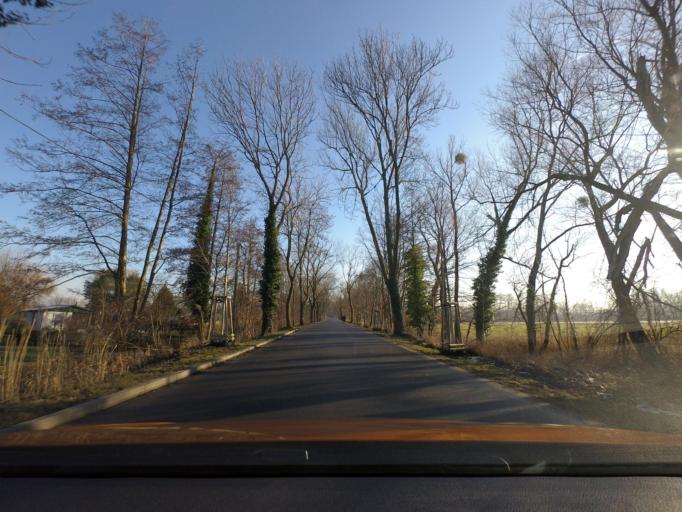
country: DE
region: Brandenburg
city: Werder
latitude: 52.4556
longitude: 12.9685
